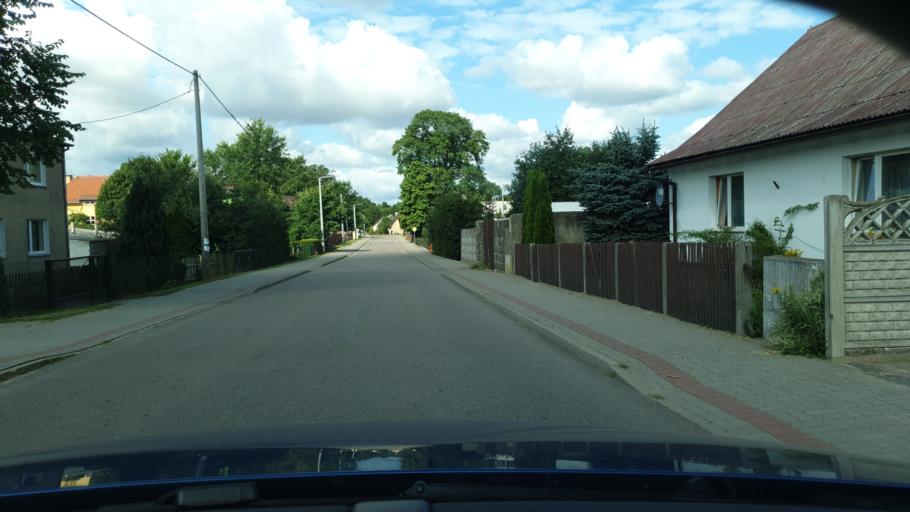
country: PL
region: Pomeranian Voivodeship
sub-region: Powiat czluchowski
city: Przechlewo
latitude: 53.8066
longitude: 17.3379
